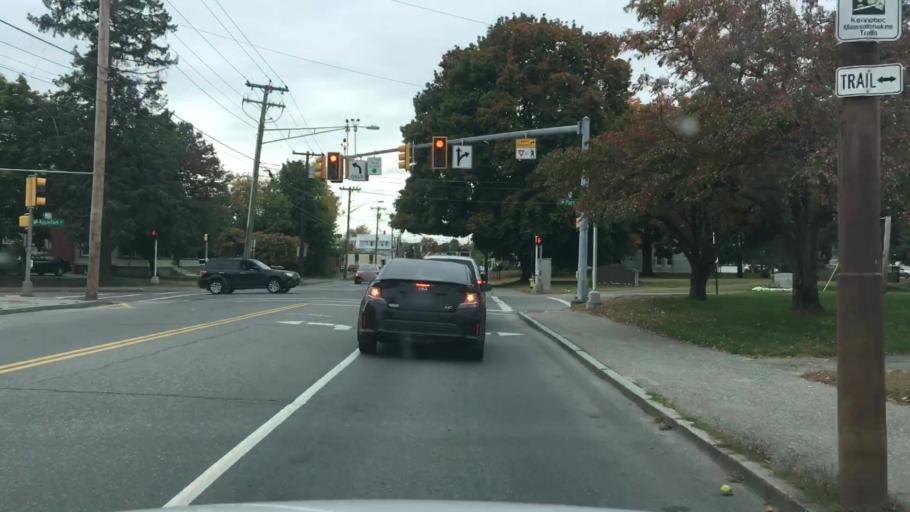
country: US
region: Maine
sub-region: Kennebec County
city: Waterville
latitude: 44.5515
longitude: -69.6324
